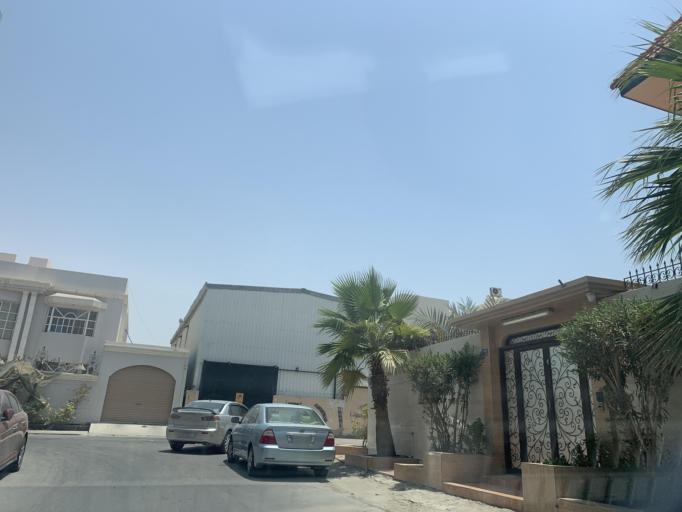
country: BH
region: Northern
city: Madinat `Isa
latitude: 26.1942
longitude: 50.4852
